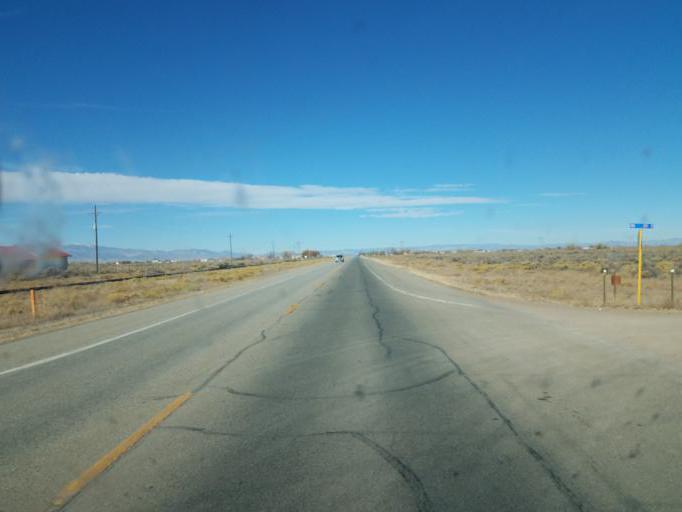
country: US
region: Colorado
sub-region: Alamosa County
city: Alamosa
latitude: 37.4981
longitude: -105.9485
